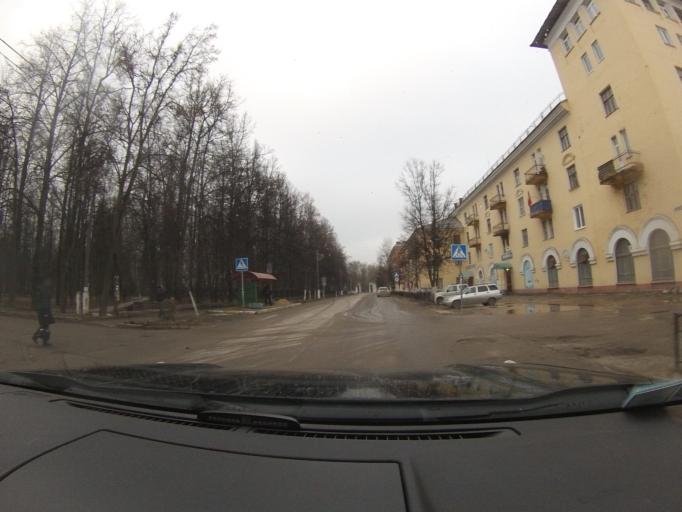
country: RU
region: Moskovskaya
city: Peski
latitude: 55.2510
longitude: 38.7582
